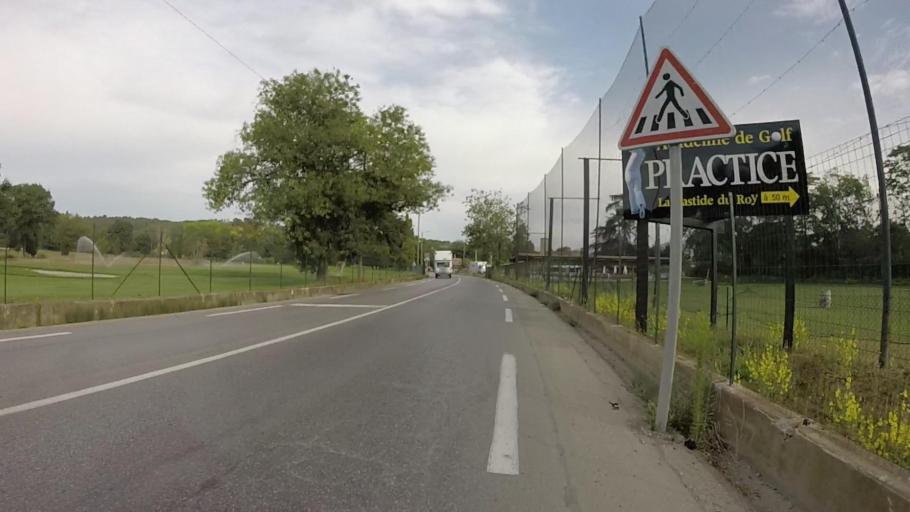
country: FR
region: Provence-Alpes-Cote d'Azur
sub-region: Departement des Alpes-Maritimes
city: Biot
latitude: 43.6164
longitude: 7.1063
